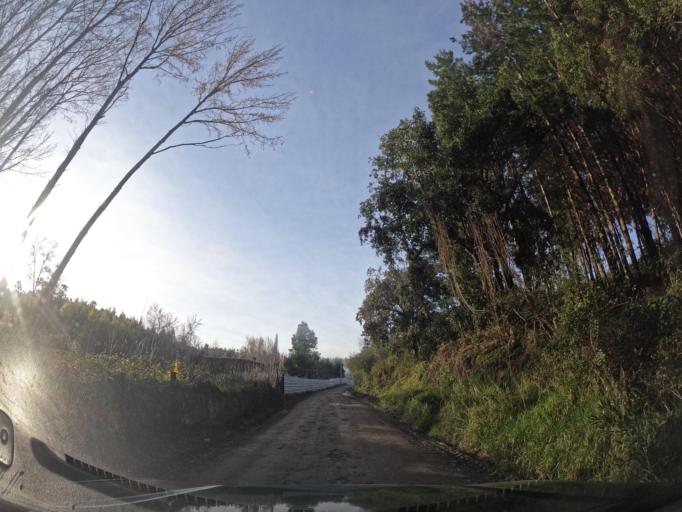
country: CL
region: Biobio
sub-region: Provincia de Concepcion
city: Concepcion
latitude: -36.8650
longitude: -72.9988
